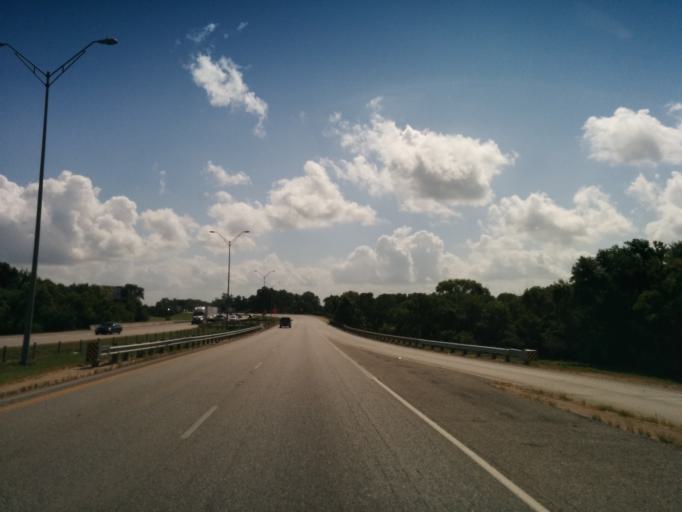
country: US
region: Texas
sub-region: Colorado County
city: Columbus
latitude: 29.6928
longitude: -96.5385
